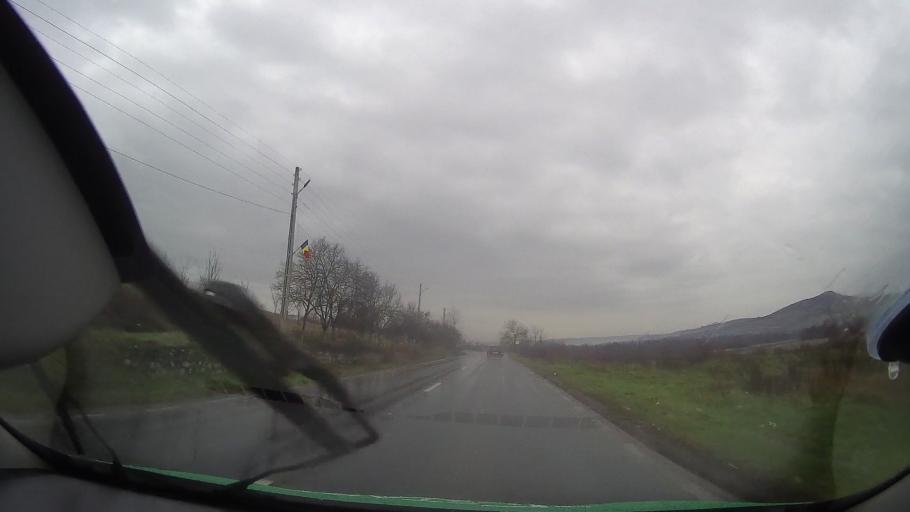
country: RO
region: Bihor
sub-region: Comuna Rabagani
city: Rabagani
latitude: 46.7574
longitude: 22.2025
